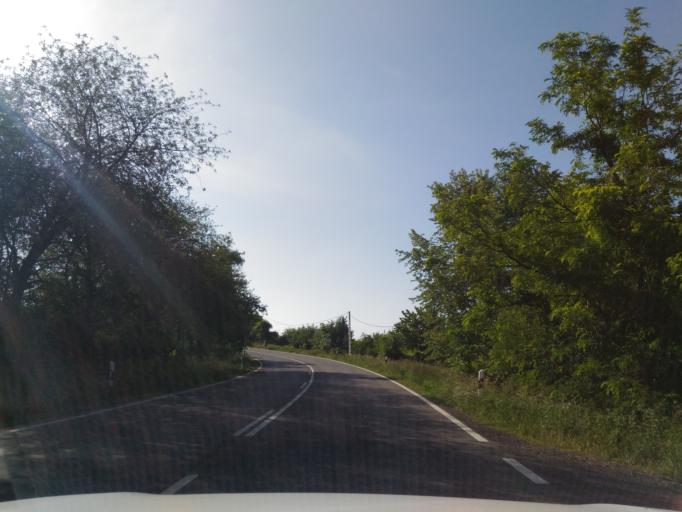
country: HU
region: Baranya
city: Komlo
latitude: 46.1765
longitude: 18.2605
